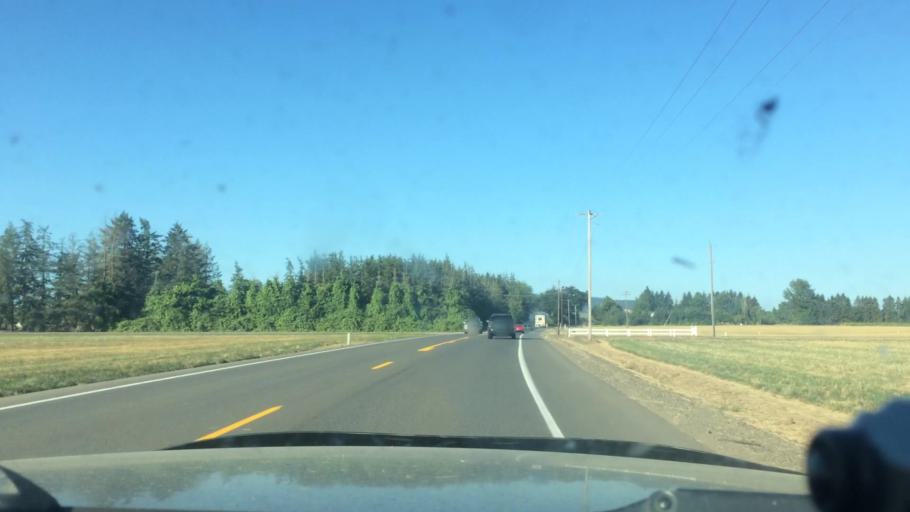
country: US
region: Oregon
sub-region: Yamhill County
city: Newberg
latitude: 45.2405
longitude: -122.9542
